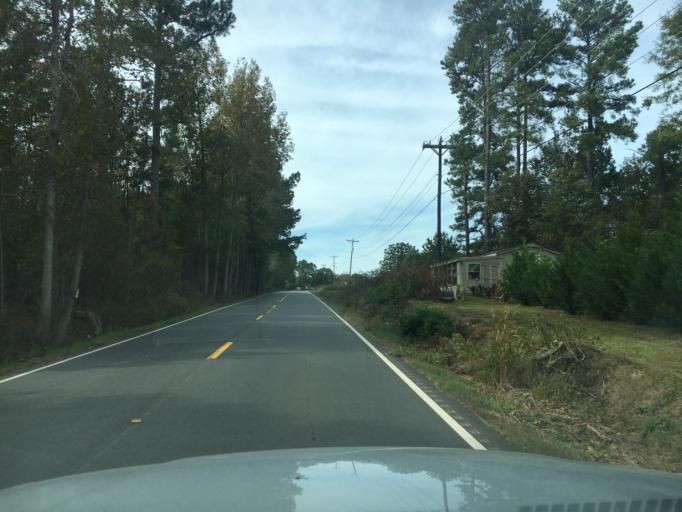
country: US
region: South Carolina
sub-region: Spartanburg County
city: Duncan
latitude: 34.8876
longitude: -82.1326
